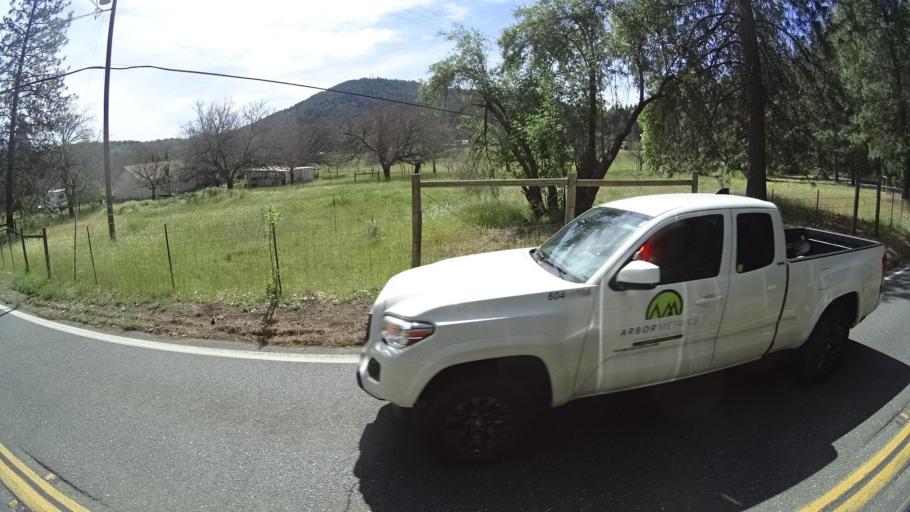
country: US
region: California
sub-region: Lake County
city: Cobb
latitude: 38.8795
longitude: -122.7336
